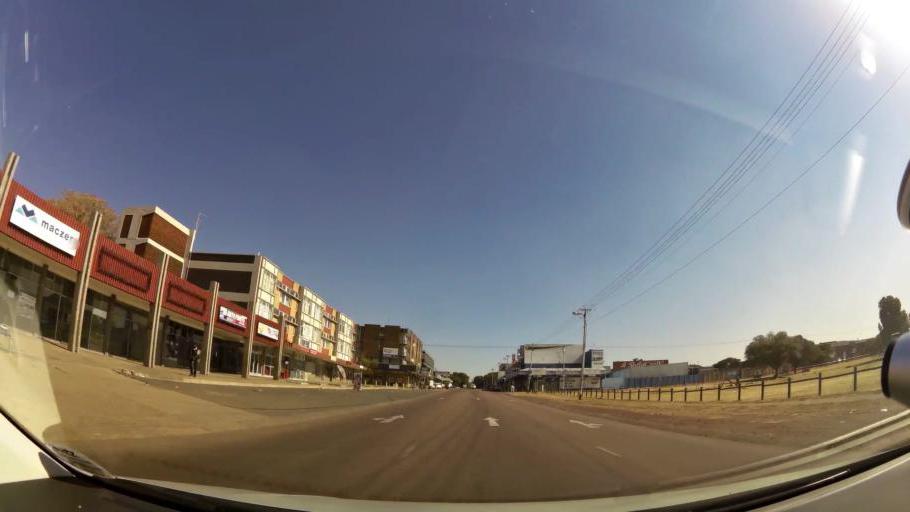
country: ZA
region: Gauteng
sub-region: City of Tshwane Metropolitan Municipality
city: Pretoria
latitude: -25.7554
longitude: 28.1512
